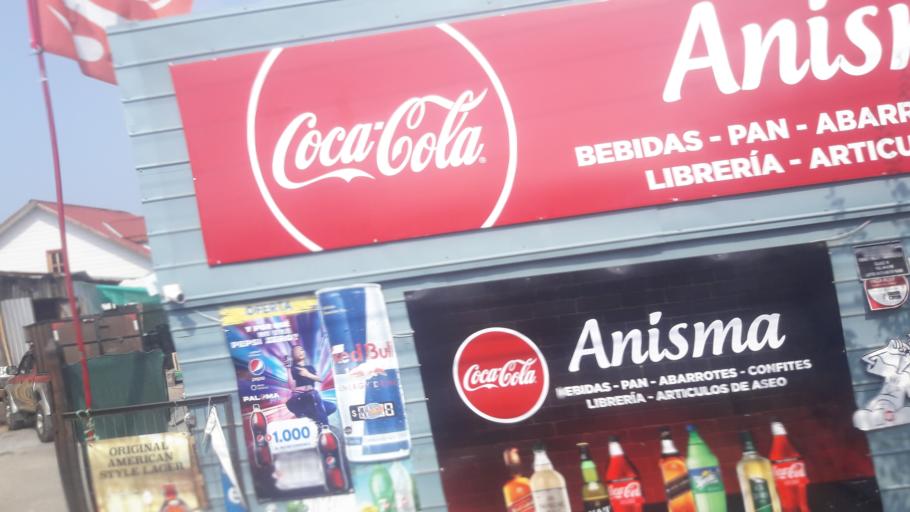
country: CL
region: Biobio
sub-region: Provincia de Concepcion
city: Lota
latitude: -37.1760
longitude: -72.9379
